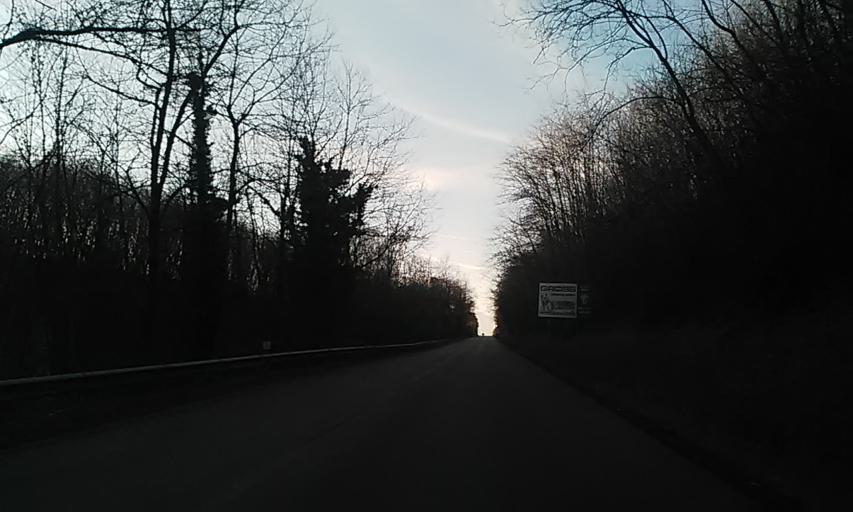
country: IT
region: Piedmont
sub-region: Provincia di Biella
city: Masserano
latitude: 45.5666
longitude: 8.2220
